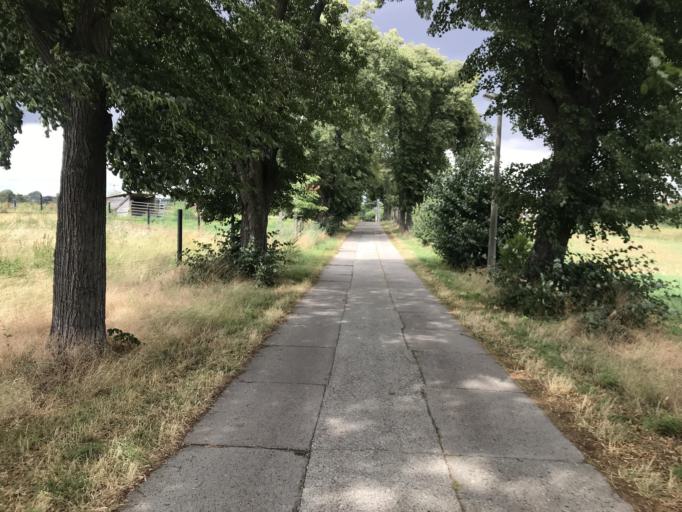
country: DE
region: Saxony-Anhalt
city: Derenburg
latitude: 51.8666
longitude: 10.9169
